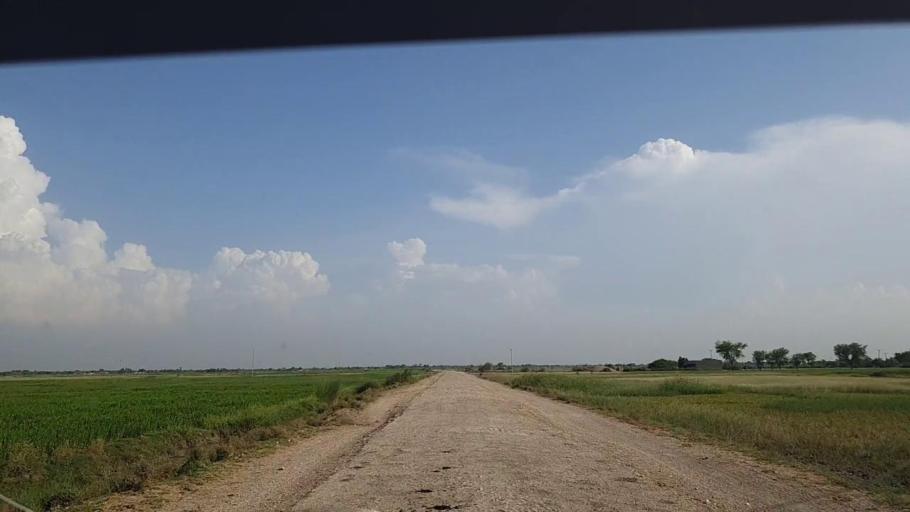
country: PK
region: Sindh
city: Khanpur
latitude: 27.8612
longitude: 69.3754
